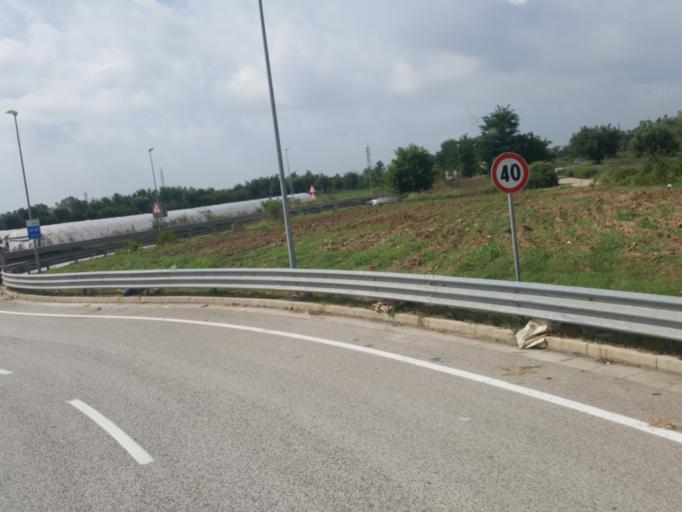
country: IT
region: Campania
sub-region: Provincia di Caserta
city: Pignataro Maggiore
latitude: 41.1809
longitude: 14.1569
